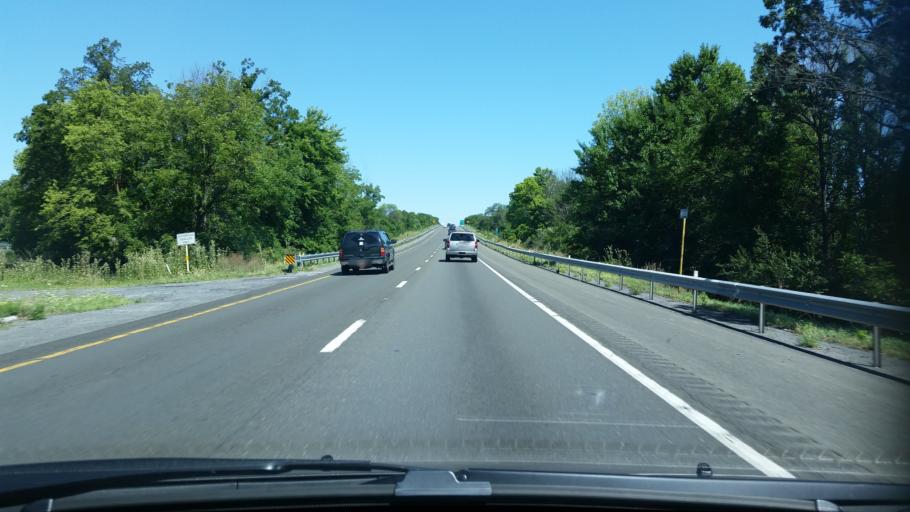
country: US
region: Virginia
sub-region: City of Winchester
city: Winchester
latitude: 39.2052
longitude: -78.1352
